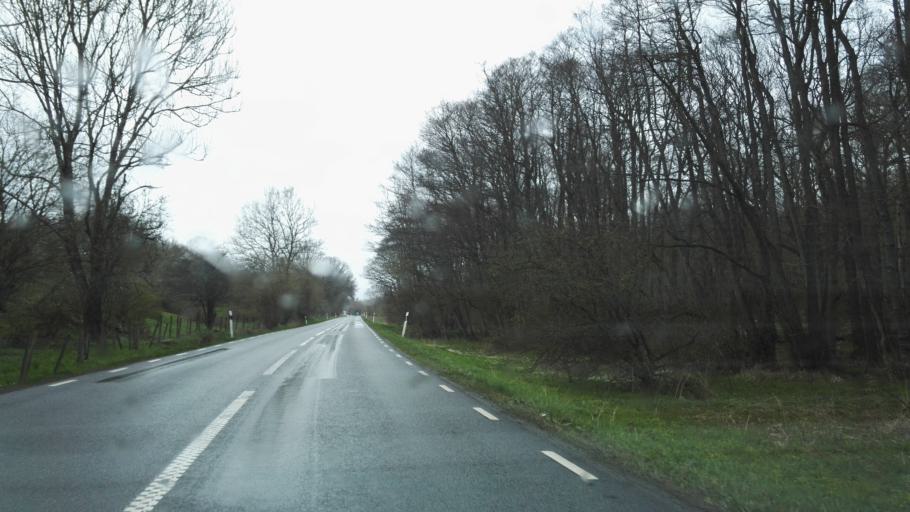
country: SE
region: Skane
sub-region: Simrishamns Kommun
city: Kivik
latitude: 55.6559
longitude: 14.2189
